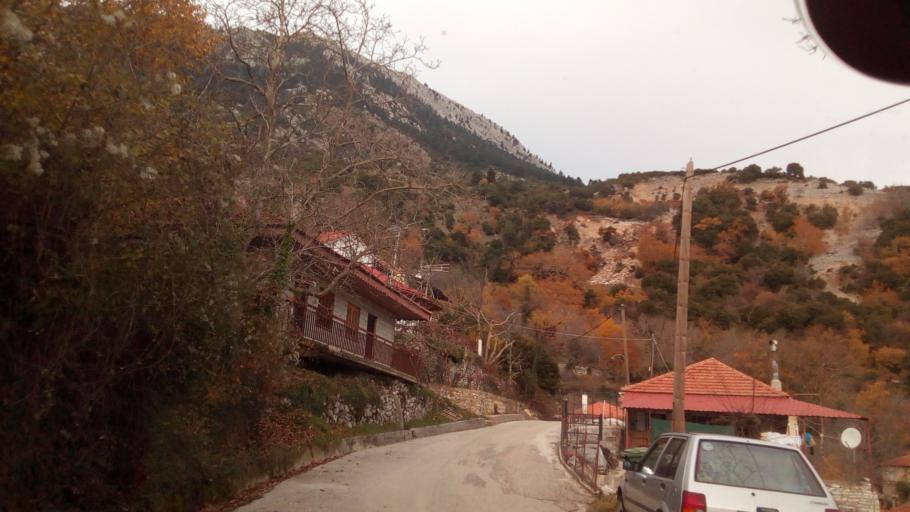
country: GR
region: West Greece
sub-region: Nomos Aitolias kai Akarnanias
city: Thermo
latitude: 38.6797
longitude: 21.8960
